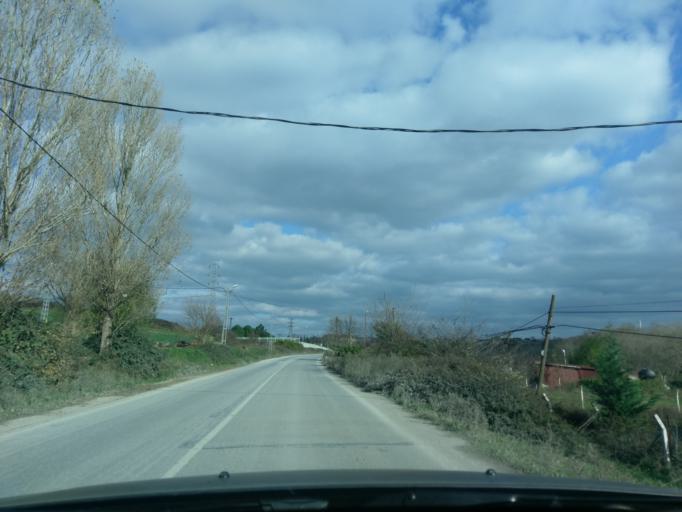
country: TR
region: Istanbul
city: Durusu
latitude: 41.2961
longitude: 28.6687
